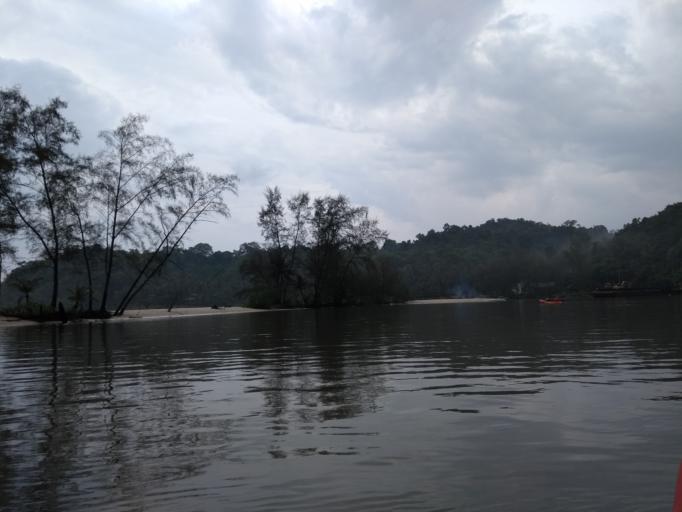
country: TH
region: Trat
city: Ko Kut
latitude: 11.6358
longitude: 102.5450
